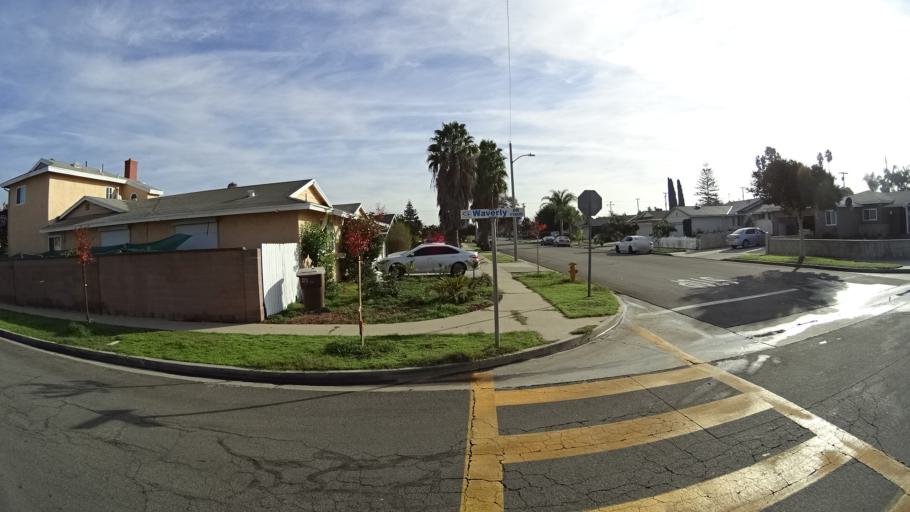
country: US
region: California
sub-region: Orange County
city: Garden Grove
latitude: 33.7916
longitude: -117.9342
